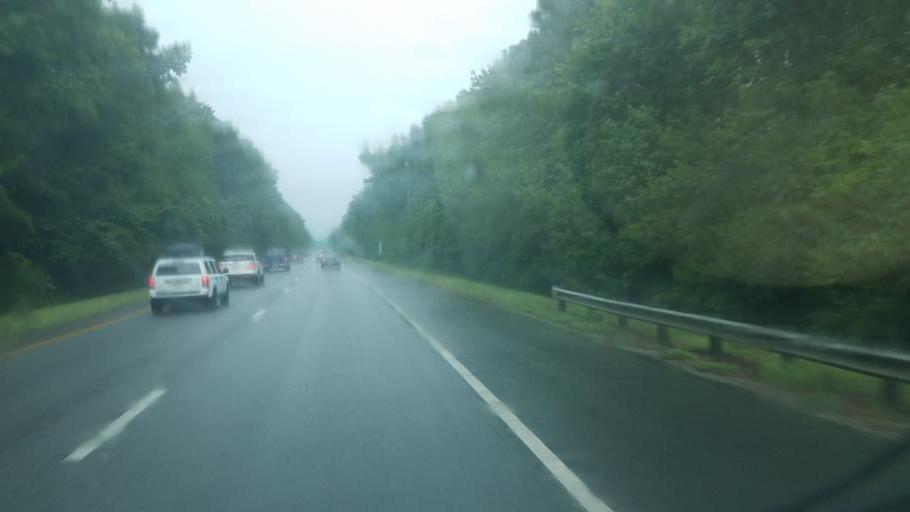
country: US
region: Virginia
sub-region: City of Portsmouth
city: Portsmouth Heights
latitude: 36.7760
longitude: -76.3716
